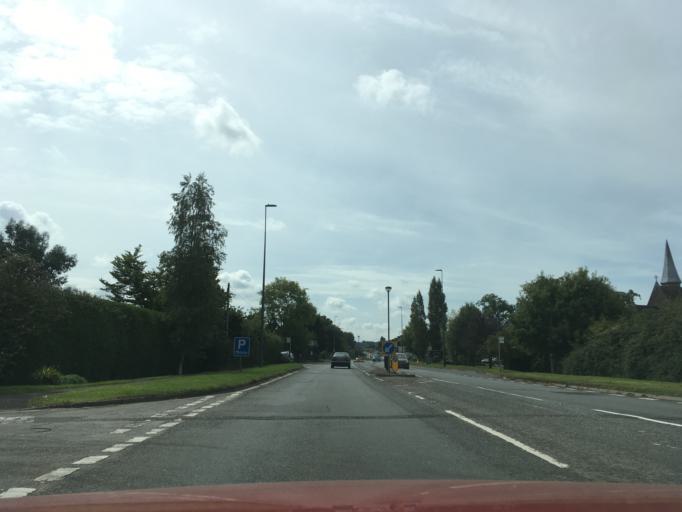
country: GB
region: England
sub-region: South Gloucestershire
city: Falfield
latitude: 51.6378
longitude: -2.4585
